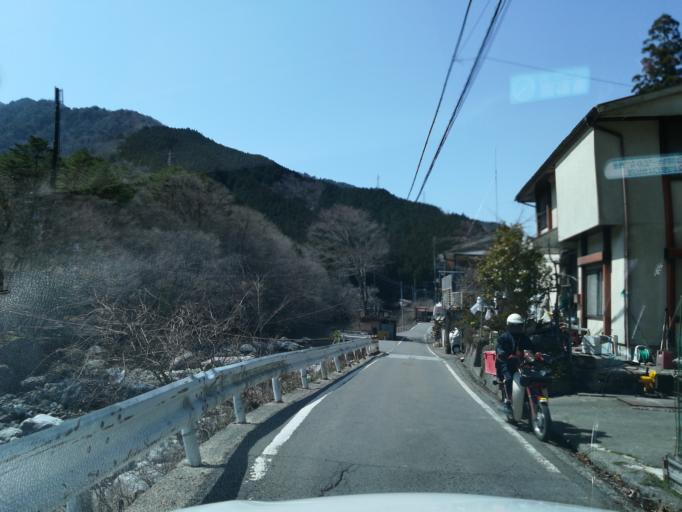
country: JP
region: Tokushima
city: Wakimachi
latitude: 33.8526
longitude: 134.0236
